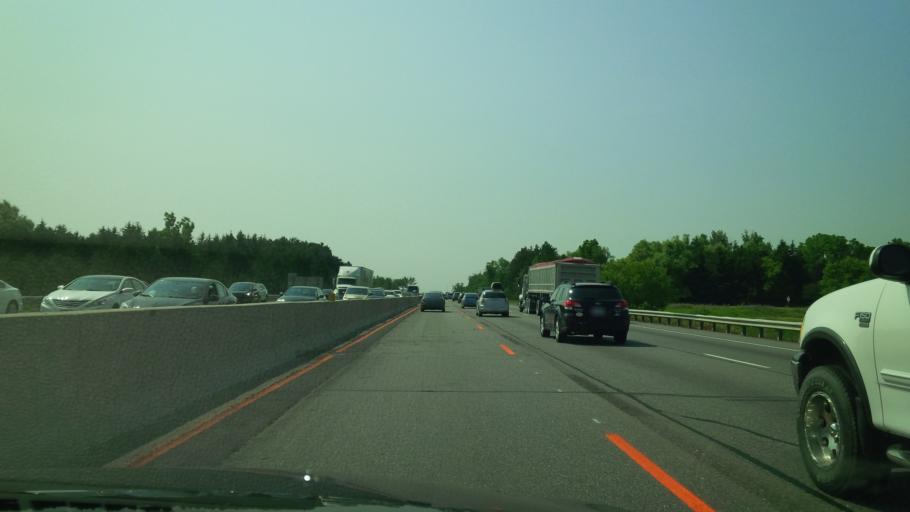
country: CA
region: Ontario
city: Bradford West Gwillimbury
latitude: 44.0128
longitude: -79.5898
